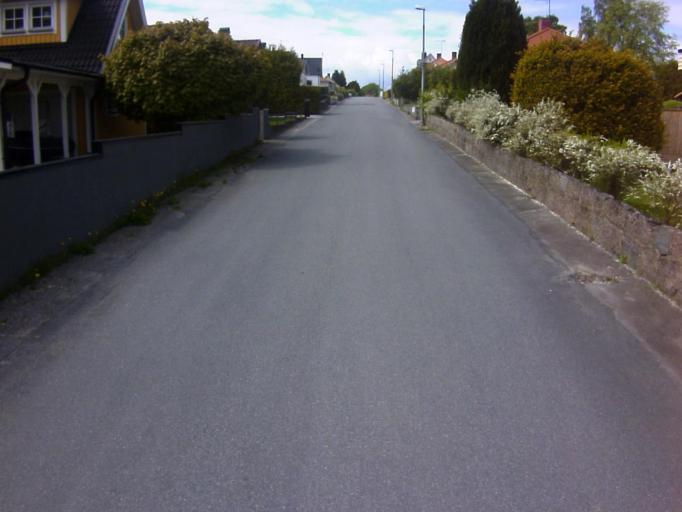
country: SE
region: Blekinge
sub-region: Solvesborgs Kommun
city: Soelvesborg
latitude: 56.0451
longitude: 14.5754
